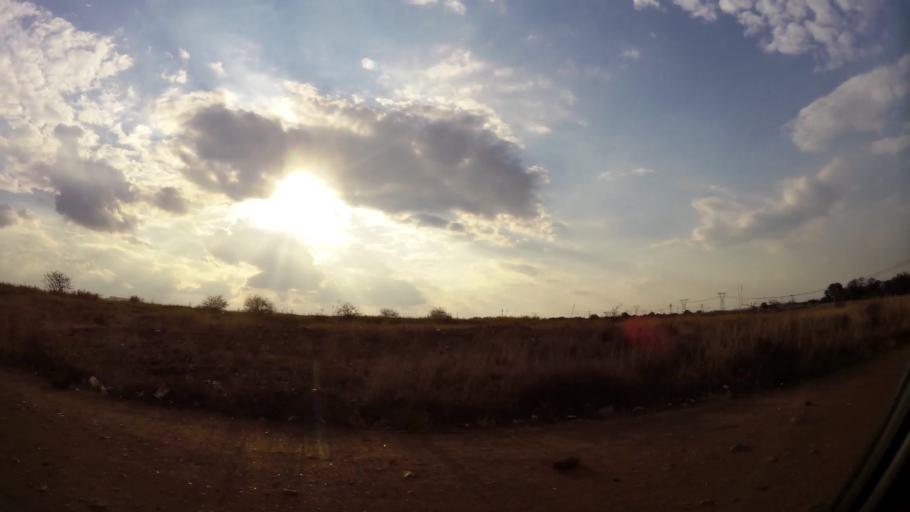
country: ZA
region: Gauteng
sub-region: Sedibeng District Municipality
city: Vereeniging
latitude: -26.6517
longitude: 27.8748
